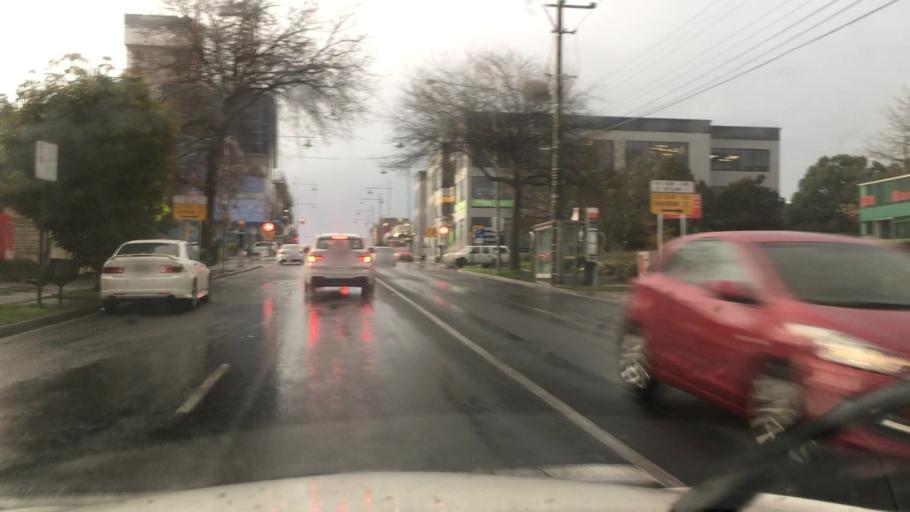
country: AU
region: Victoria
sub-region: Whitehorse
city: Box Hill
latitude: -37.8219
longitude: 145.1231
